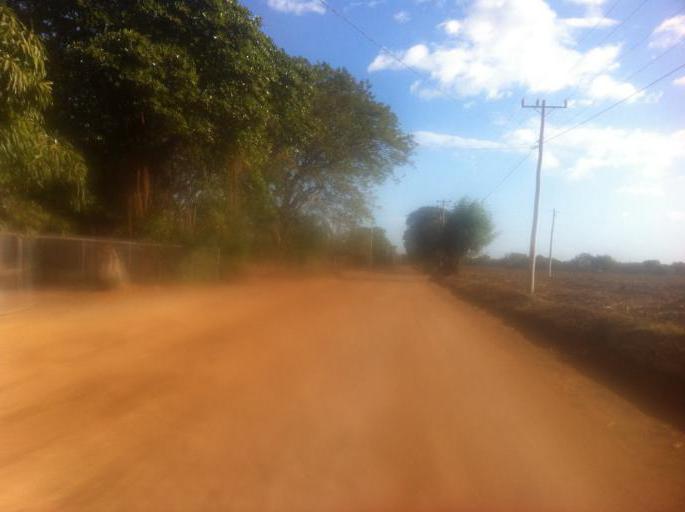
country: NI
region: Managua
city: Carlos Fonseca Amador
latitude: 11.8968
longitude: -86.5872
